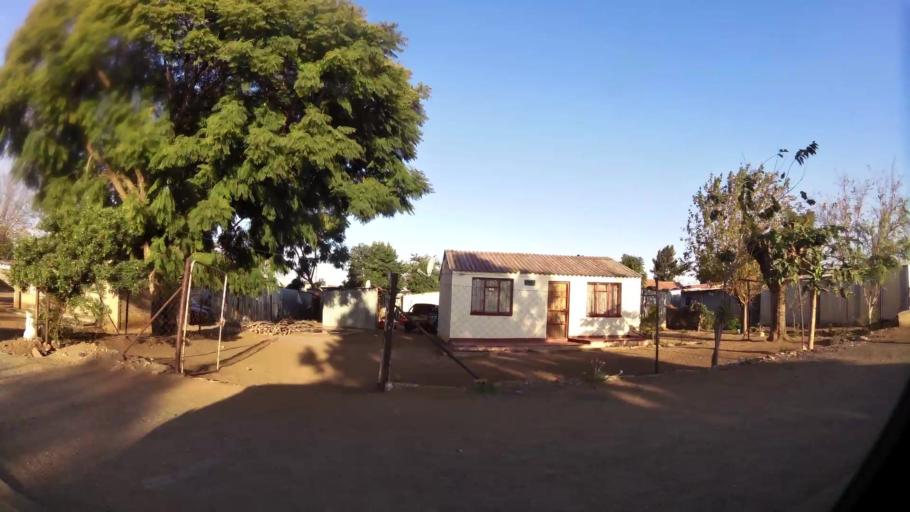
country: ZA
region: North-West
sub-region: Bojanala Platinum District Municipality
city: Rustenburg
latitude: -25.6314
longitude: 27.2108
